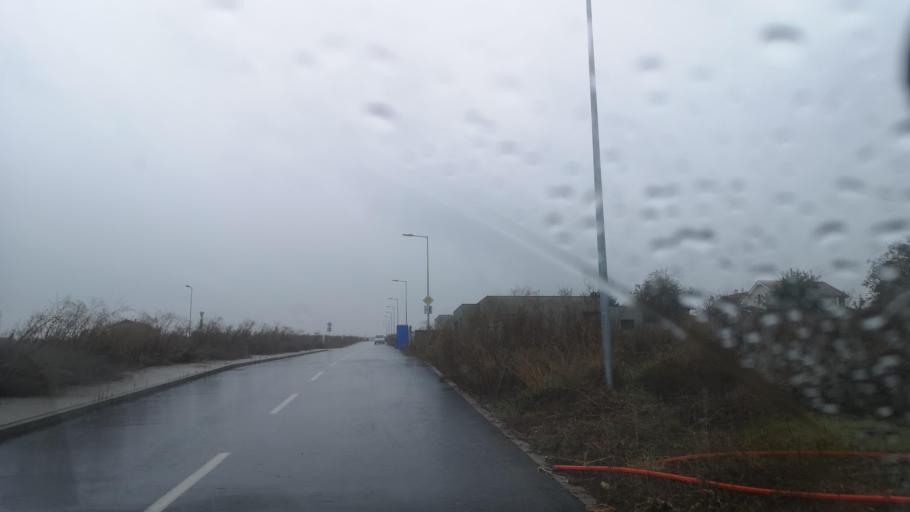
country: SK
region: Nitriansky
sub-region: Okres Nitra
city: Nitra
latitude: 48.2942
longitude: 18.1296
